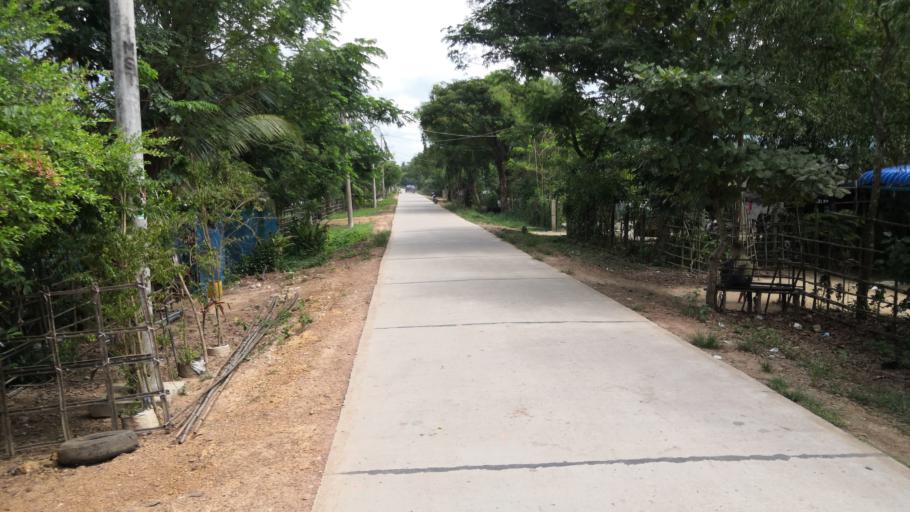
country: MM
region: Yangon
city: Kanbe
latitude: 16.4350
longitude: 96.1610
